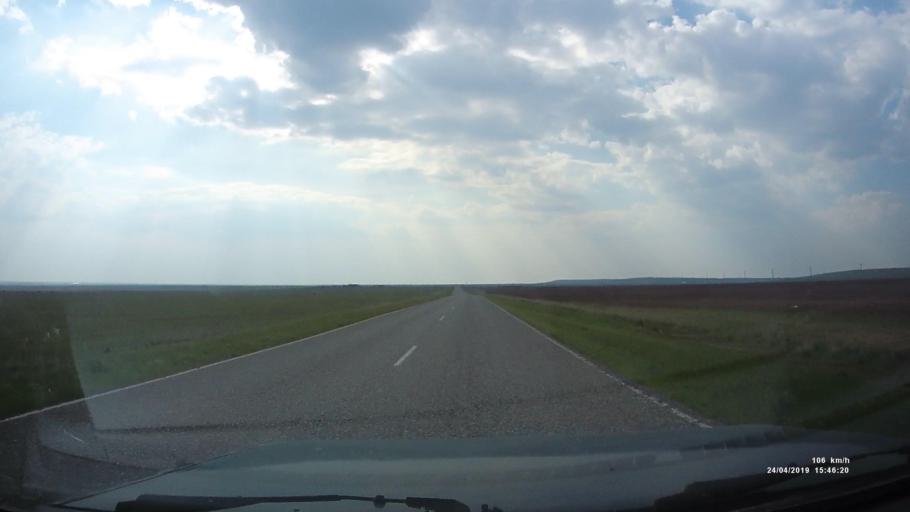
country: RU
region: Kalmykiya
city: Yashalta
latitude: 46.5927
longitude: 42.7171
